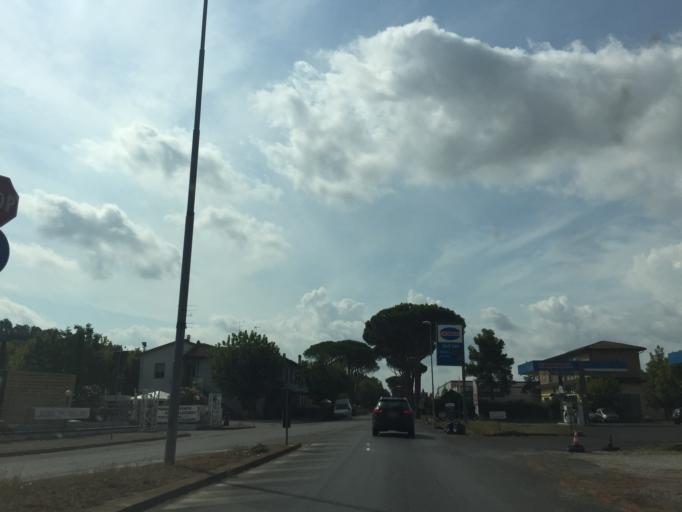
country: IT
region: Tuscany
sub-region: Province of Florence
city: Cerreto Guidi
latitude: 43.7423
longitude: 10.9013
